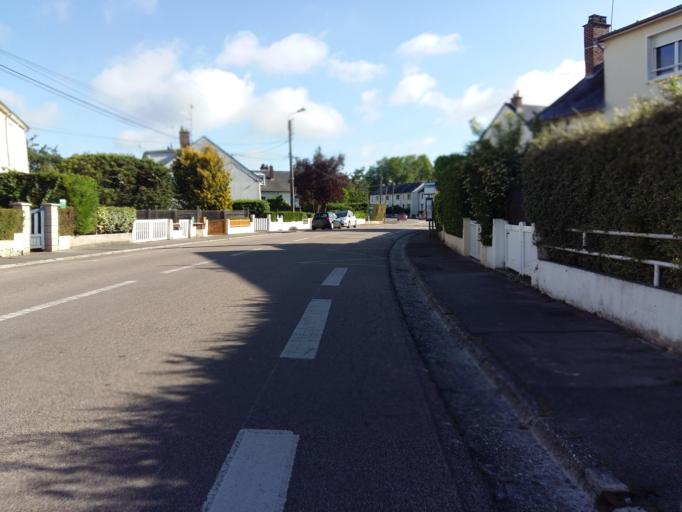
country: FR
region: Picardie
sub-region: Departement de la Somme
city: Rivery
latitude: 49.9076
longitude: 2.3265
